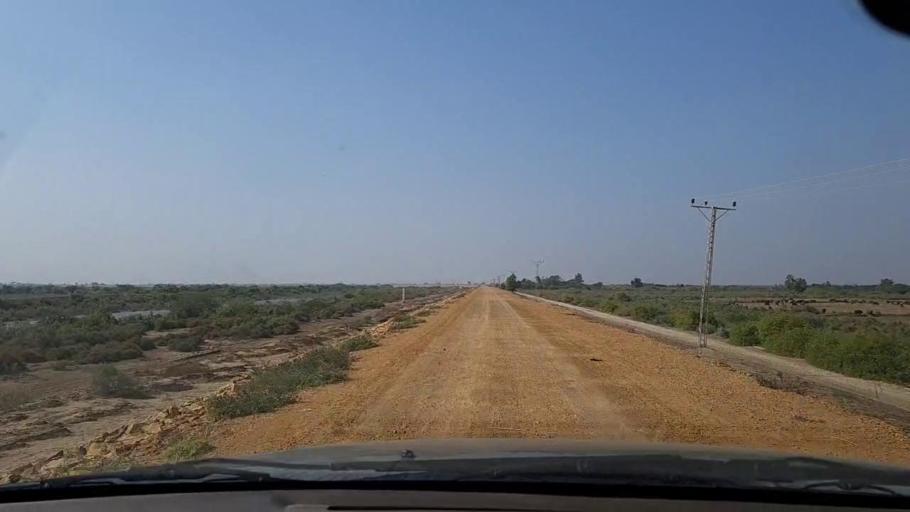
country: PK
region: Sindh
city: Chuhar Jamali
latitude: 24.4619
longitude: 67.8897
